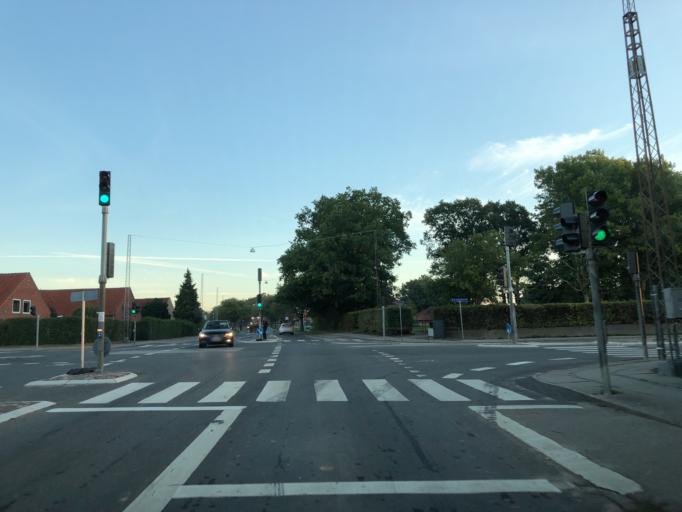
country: DK
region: South Denmark
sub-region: Sonderborg Kommune
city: Sonderborg
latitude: 54.9034
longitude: 9.8105
